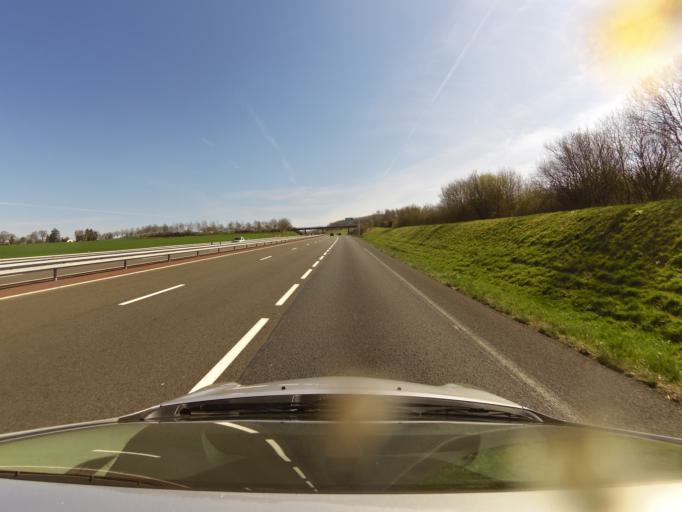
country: FR
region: Lower Normandy
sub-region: Departement de la Manche
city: Villedieu-les-Poeles
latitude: 48.8581
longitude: -1.2123
